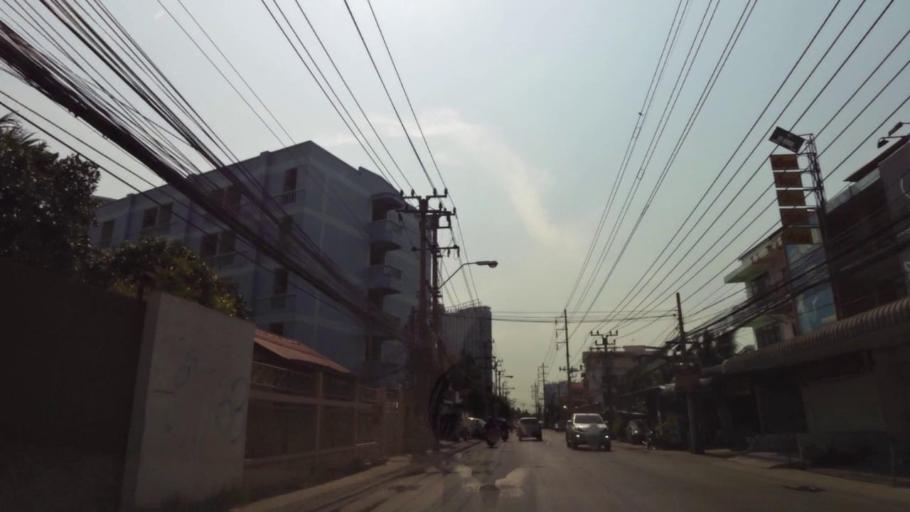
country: TH
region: Bangkok
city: Phra Khanong
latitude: 13.6521
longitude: 100.5932
